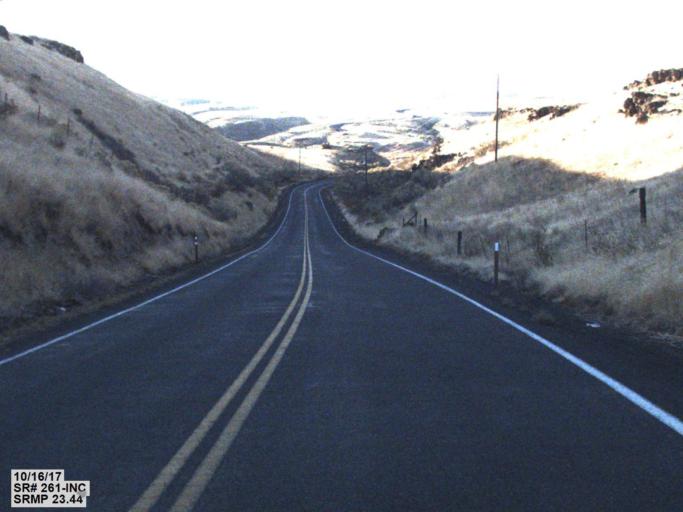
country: US
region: Washington
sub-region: Walla Walla County
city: Waitsburg
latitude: 46.6711
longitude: -118.3158
